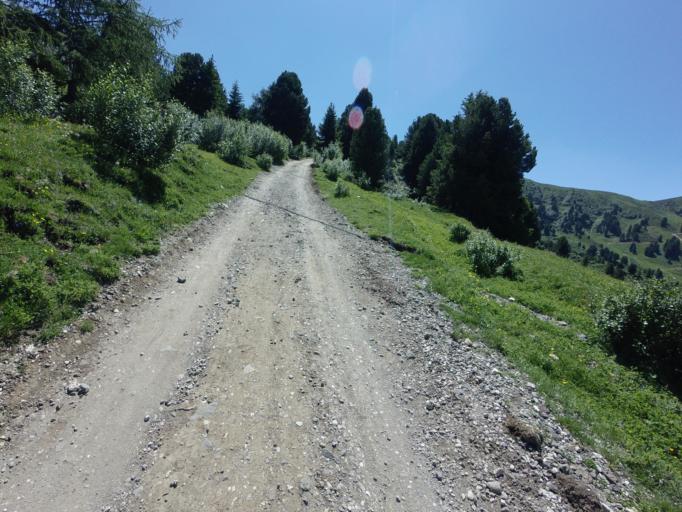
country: IT
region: Trentino-Alto Adige
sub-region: Provincia di Trento
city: Mazzin
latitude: 46.5116
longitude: 11.6912
